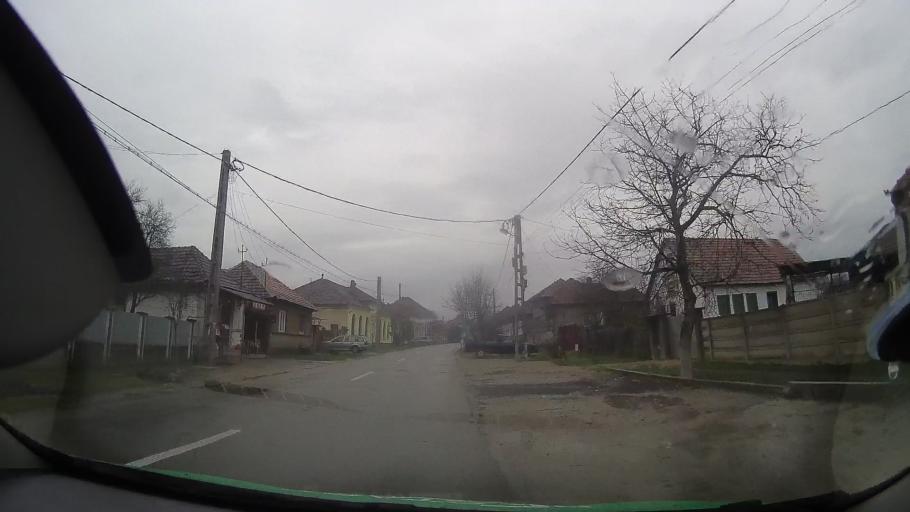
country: RO
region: Bihor
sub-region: Comuna Holod
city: Holod
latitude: 46.7850
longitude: 22.1243
